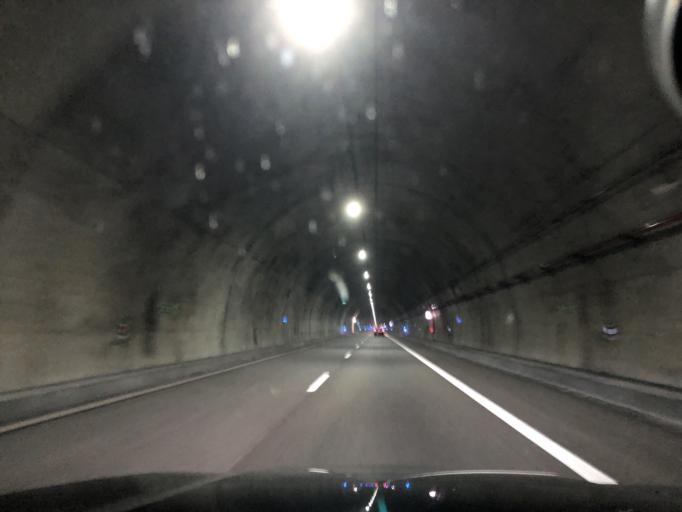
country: PT
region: Vila Real
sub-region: Mesao Frio
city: Mesao Frio
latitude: 41.2730
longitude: -7.9046
